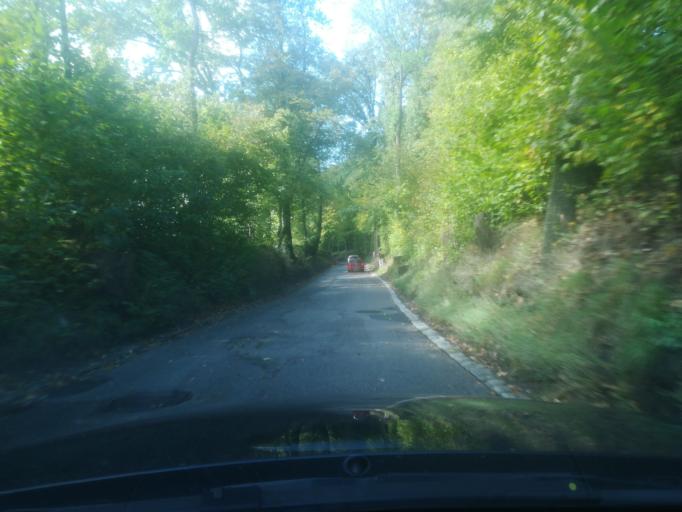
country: AT
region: Upper Austria
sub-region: Linz Stadt
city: Linz
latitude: 48.3332
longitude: 14.2859
